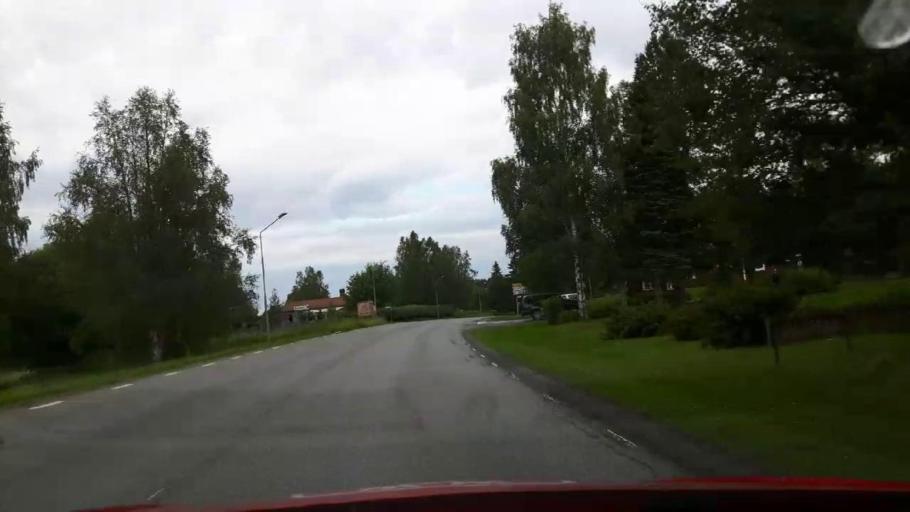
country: SE
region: Jaemtland
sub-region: Stroemsunds Kommun
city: Stroemsund
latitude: 63.5769
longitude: 15.3518
